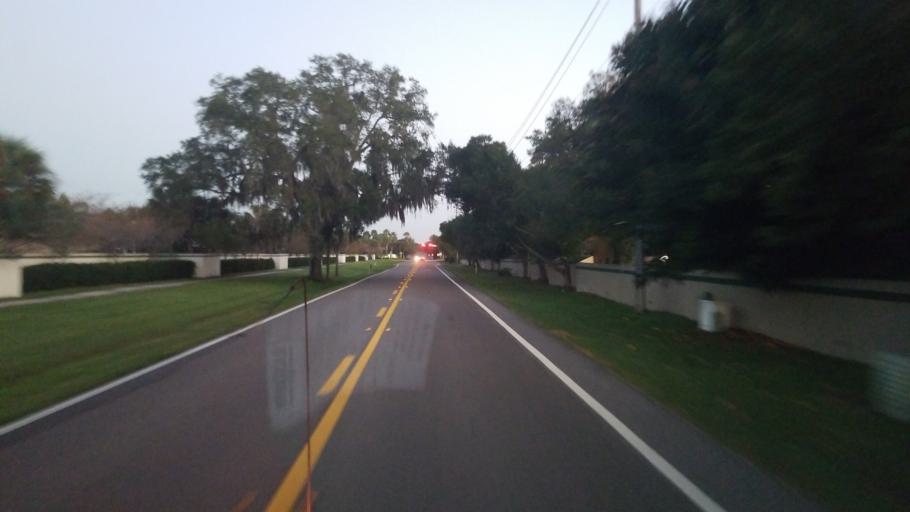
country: US
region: Florida
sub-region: Sarasota County
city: Lake Sarasota
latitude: 27.2813
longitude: -82.4563
